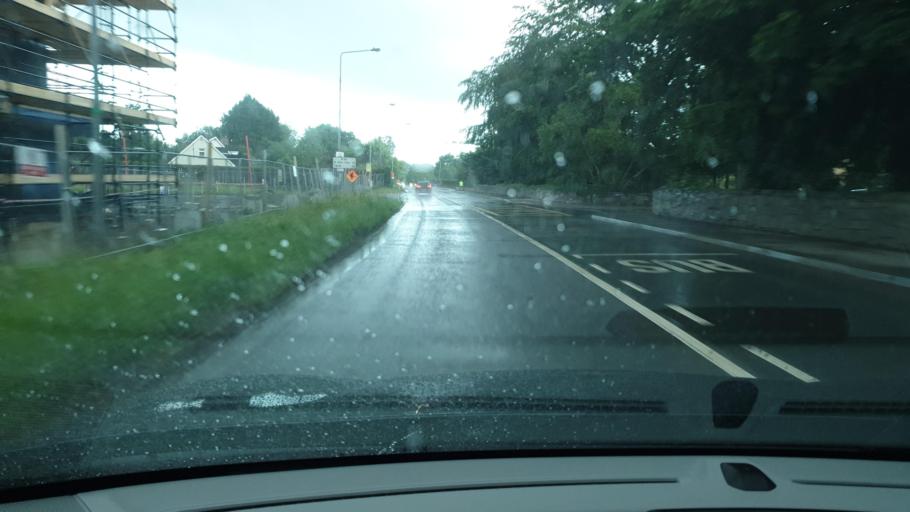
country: IE
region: Leinster
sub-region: An Mhi
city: Navan
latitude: 53.6414
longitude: -6.6886
